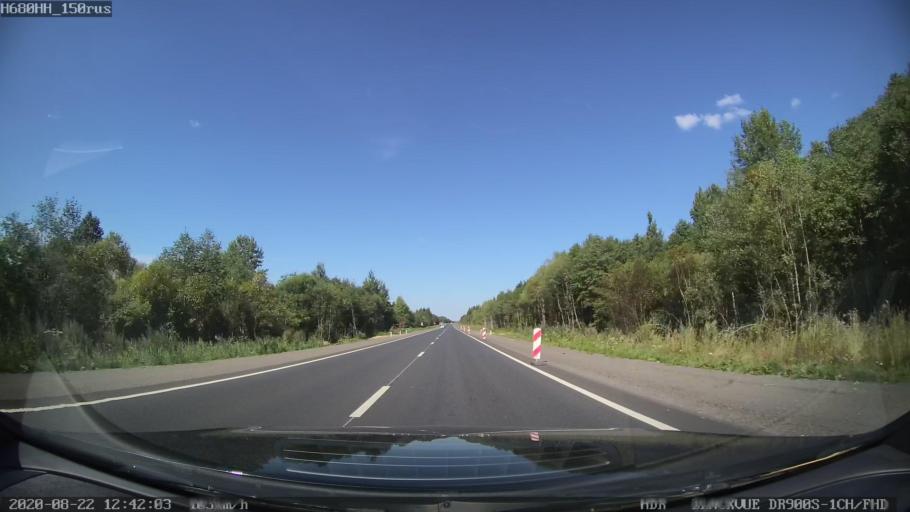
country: RU
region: Tverskaya
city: Rameshki
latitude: 57.3560
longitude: 36.0969
